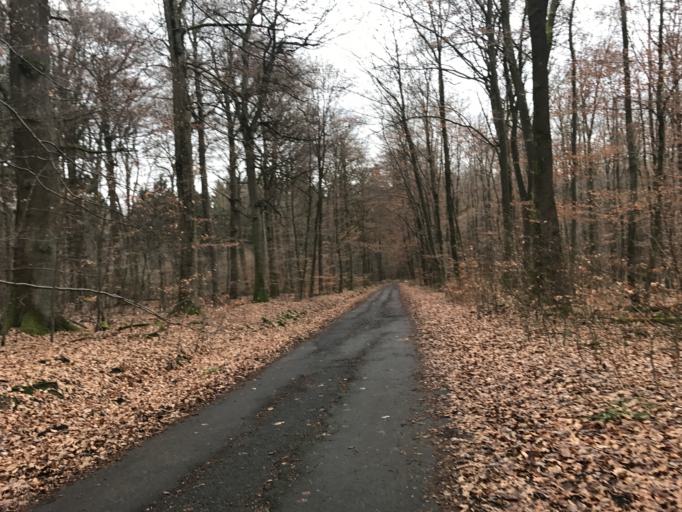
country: DE
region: Hesse
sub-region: Regierungsbezirk Darmstadt
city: Wiesbaden
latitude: 50.1221
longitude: 8.2376
